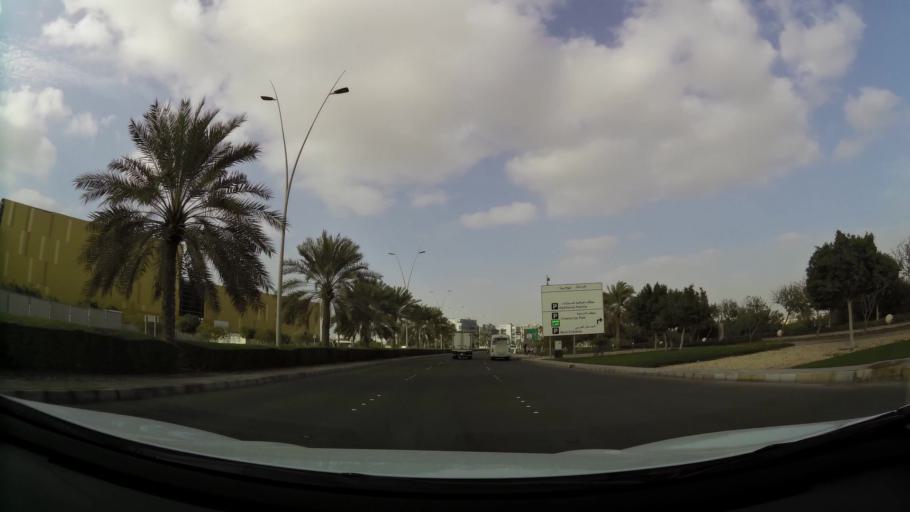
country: AE
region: Abu Dhabi
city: Abu Dhabi
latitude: 24.4898
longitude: 54.6023
